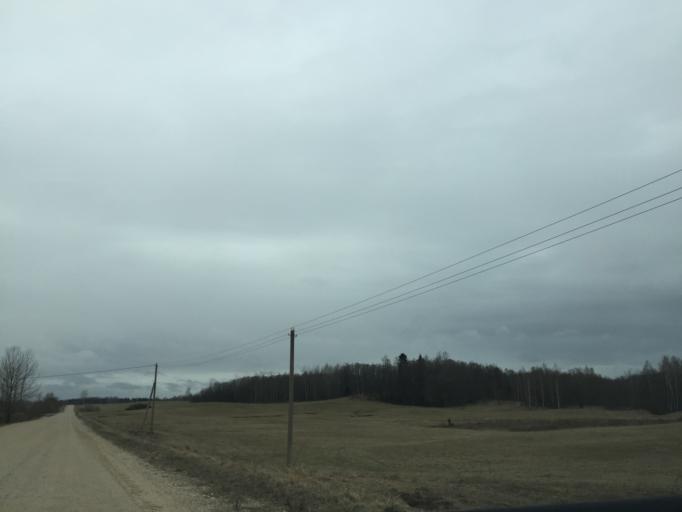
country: LV
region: Kraslavas Rajons
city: Kraslava
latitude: 55.9825
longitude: 27.1416
